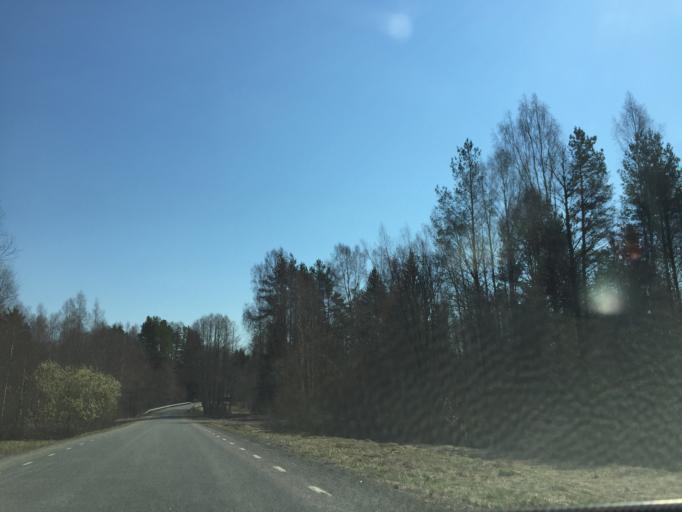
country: EE
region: Jogevamaa
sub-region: Mustvee linn
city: Mustvee
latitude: 58.5863
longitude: 26.8947
